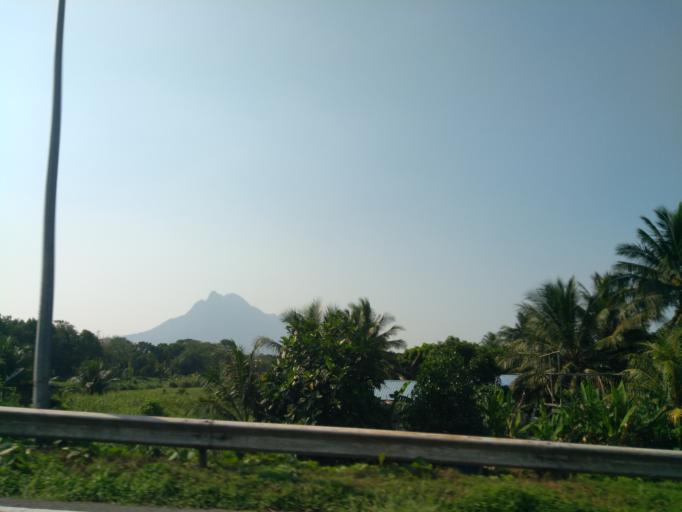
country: MY
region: Sarawak
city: Kuching
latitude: 1.6798
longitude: 110.3419
